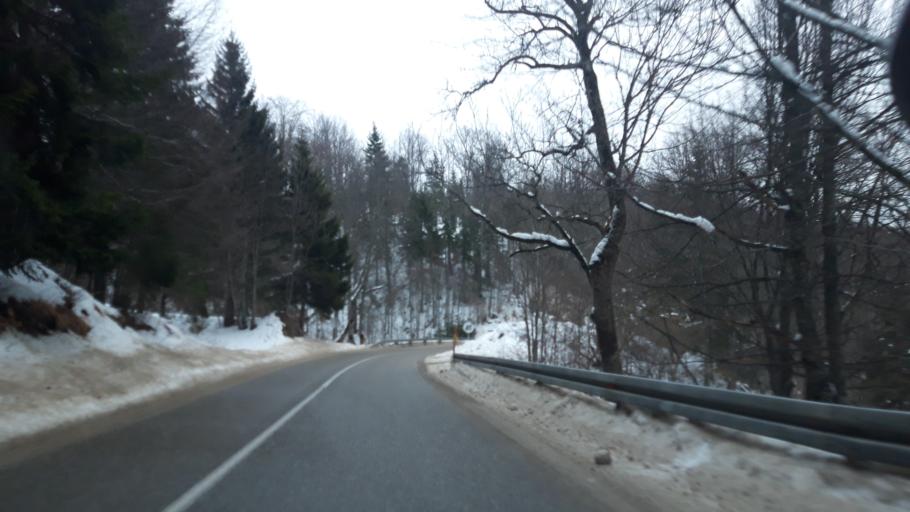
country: BA
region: Republika Srpska
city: Han Pijesak
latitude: 44.1317
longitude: 18.9558
